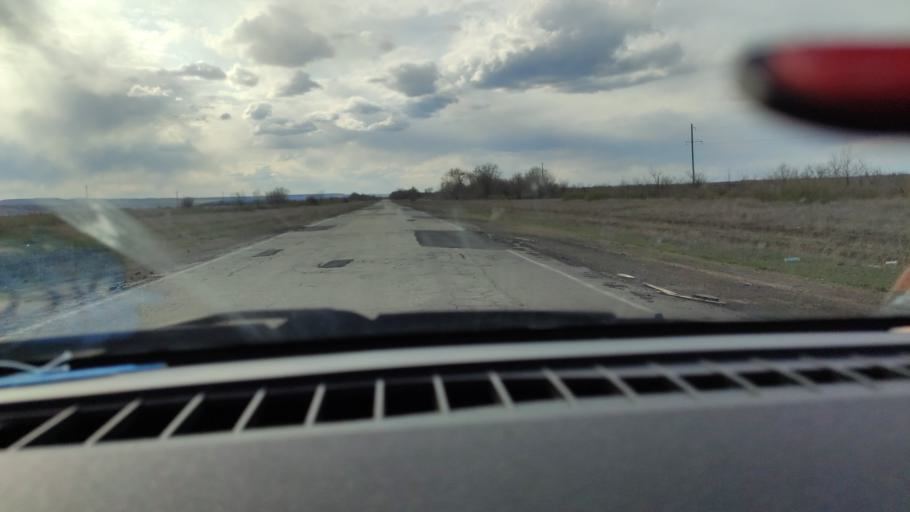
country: RU
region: Saratov
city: Rovnoye
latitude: 51.0664
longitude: 46.0047
